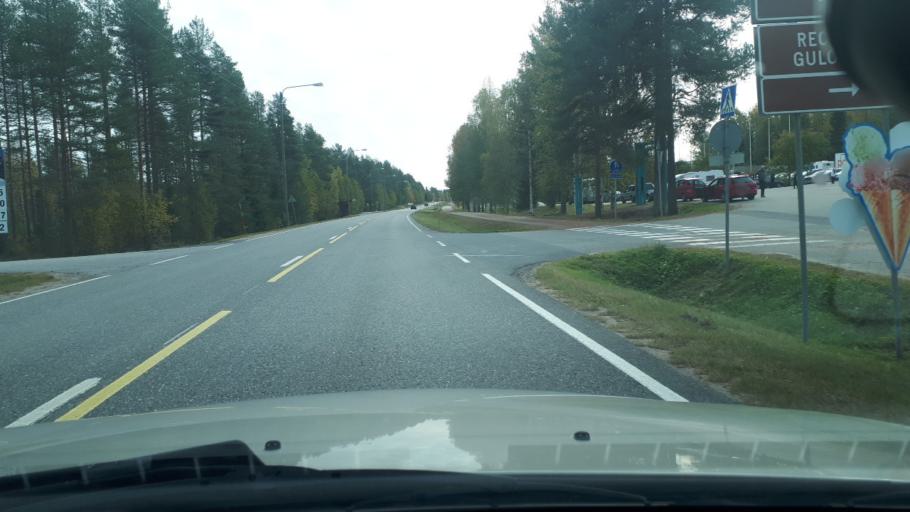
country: FI
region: Lapland
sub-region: Rovaniemi
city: Ranua
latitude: 65.9445
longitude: 26.4661
